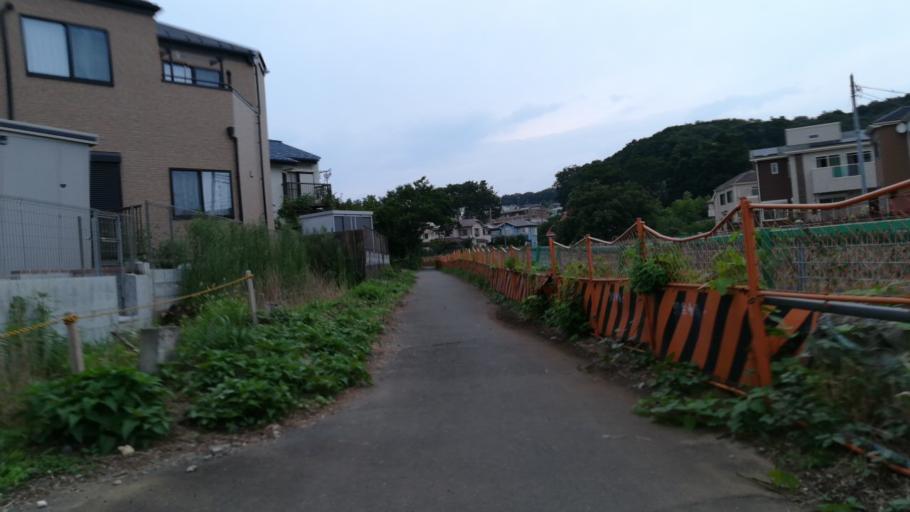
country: JP
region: Tokyo
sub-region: Machida-shi
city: Machida
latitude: 35.5831
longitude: 139.3996
